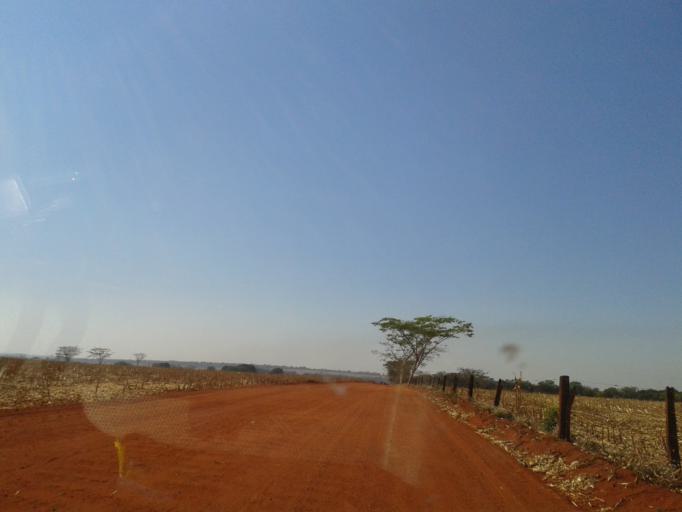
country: BR
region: Minas Gerais
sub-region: Capinopolis
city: Capinopolis
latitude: -18.5994
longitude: -49.5129
